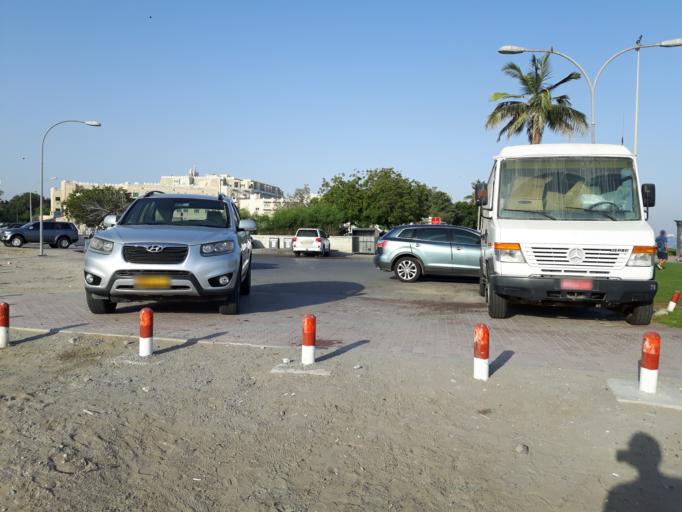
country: OM
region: Muhafazat Masqat
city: Bawshar
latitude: 23.6106
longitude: 58.4468
